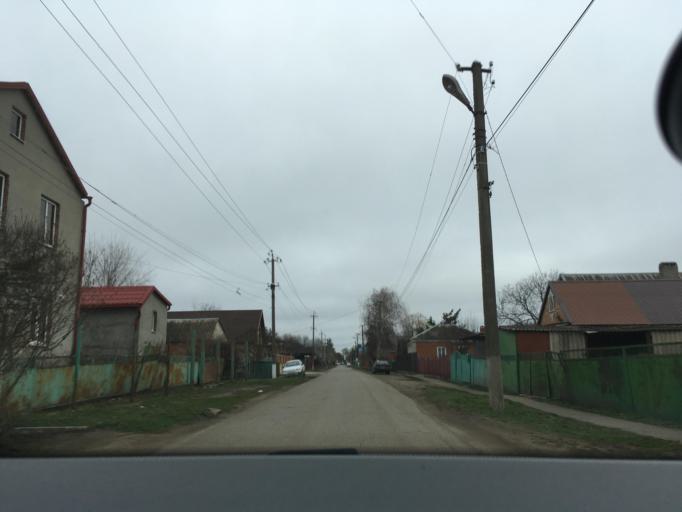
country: RU
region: Krasnodarskiy
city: Kushchevskaya
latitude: 46.5742
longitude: 39.6244
